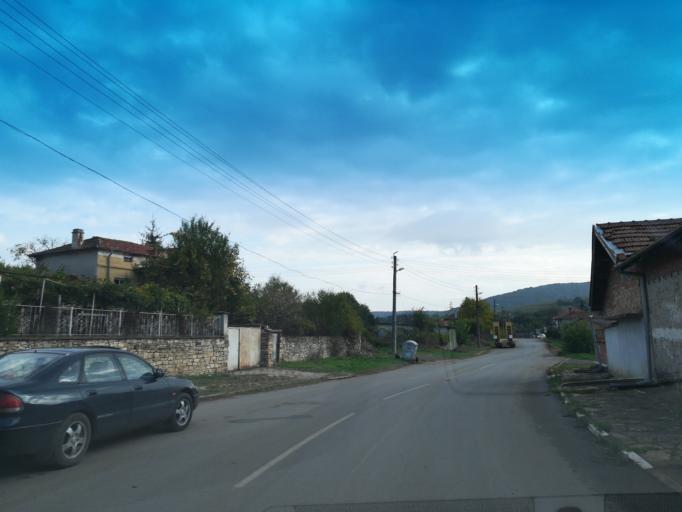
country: BG
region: Stara Zagora
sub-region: Obshtina Nikolaevo
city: Elkhovo
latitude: 42.3409
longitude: 25.4014
